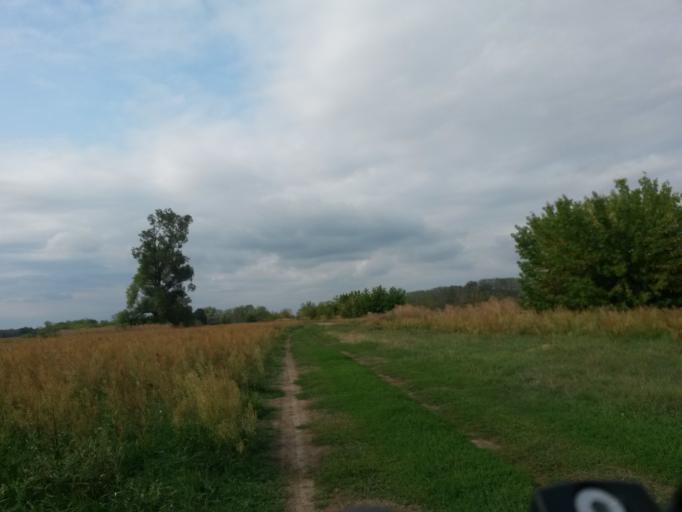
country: DE
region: Saxony-Anhalt
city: Tangermunde
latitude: 52.5270
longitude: 11.9702
